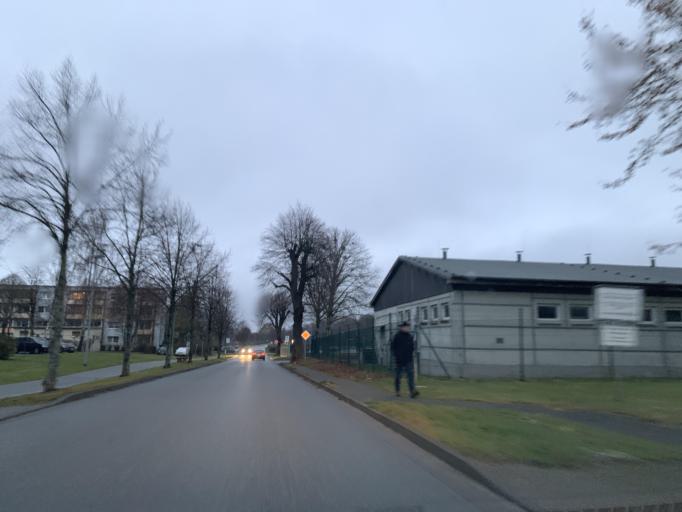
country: DE
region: Mecklenburg-Vorpommern
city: Burg Stargard
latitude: 53.5253
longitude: 13.2843
